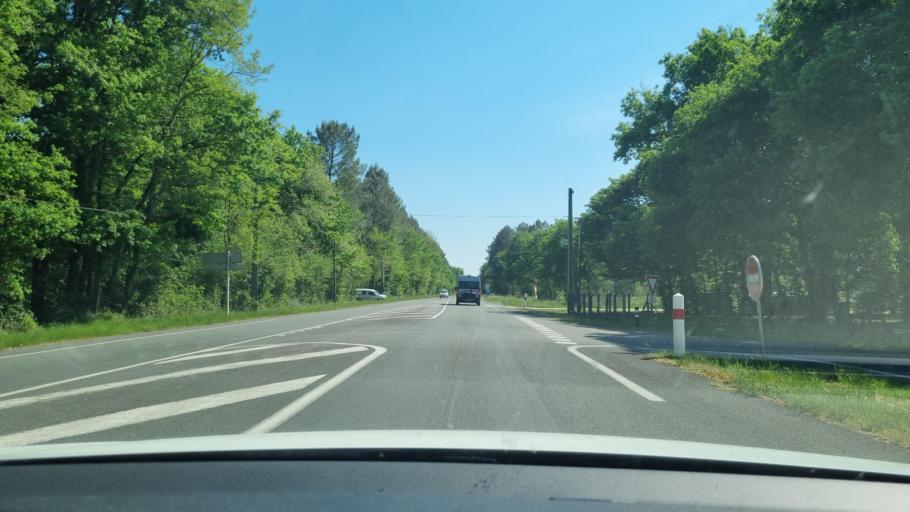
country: FR
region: Aquitaine
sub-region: Departement de la Gironde
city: Prechac
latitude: 44.2626
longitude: -0.2615
